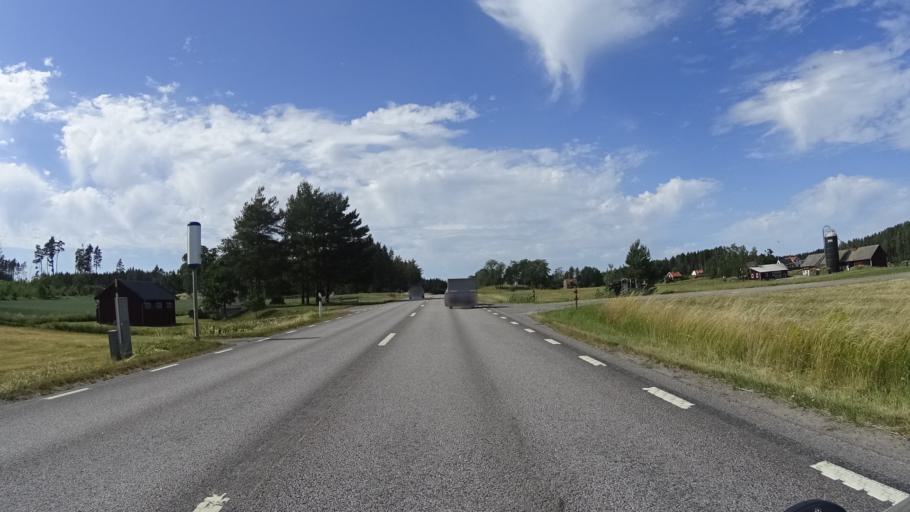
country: SE
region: OEstergoetland
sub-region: Linkopings Kommun
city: Linghem
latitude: 58.3527
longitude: 15.8350
